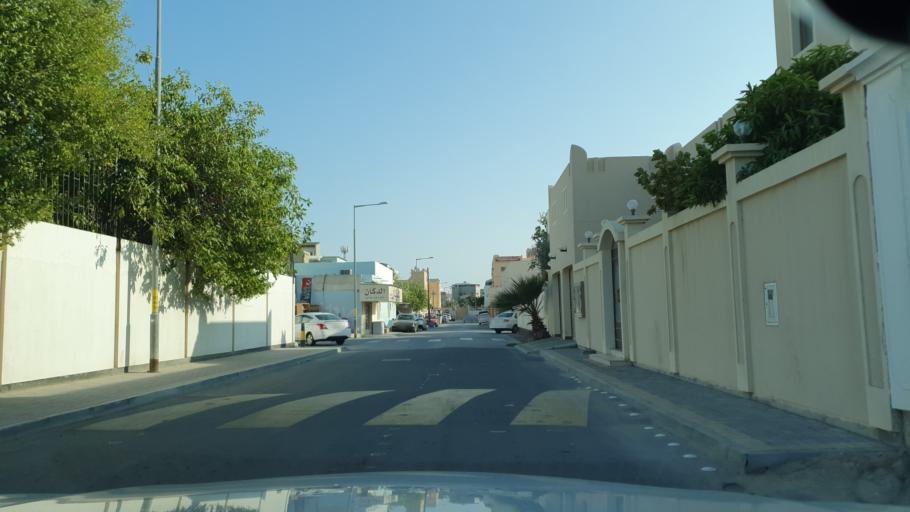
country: BH
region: Manama
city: Jidd Hafs
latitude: 26.2234
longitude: 50.4614
